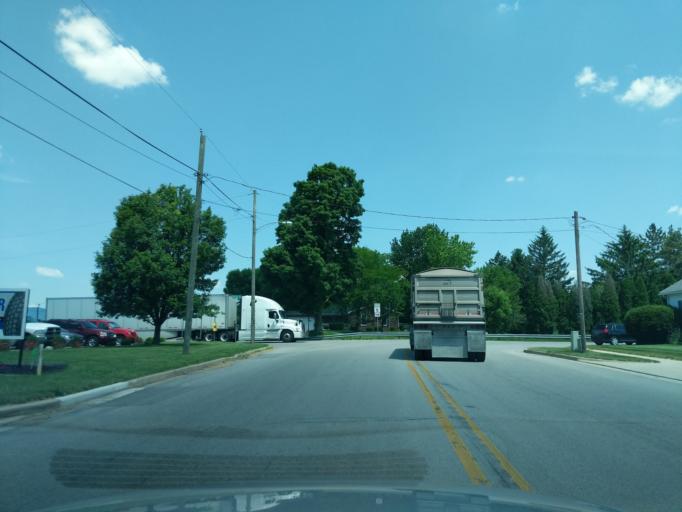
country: US
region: Indiana
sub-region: Noble County
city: Ligonier
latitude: 41.4737
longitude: -85.5880
